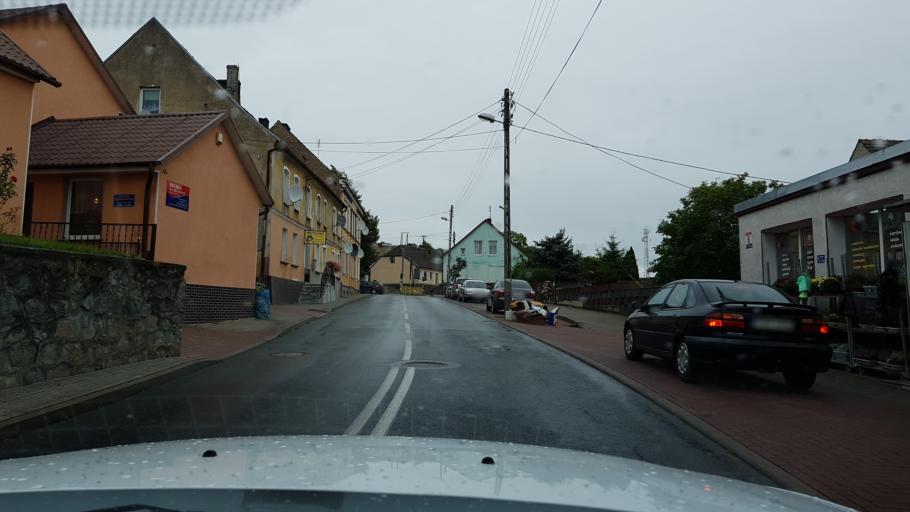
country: PL
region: West Pomeranian Voivodeship
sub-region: Powiat gryfinski
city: Cedynia
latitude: 52.8796
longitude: 14.2047
